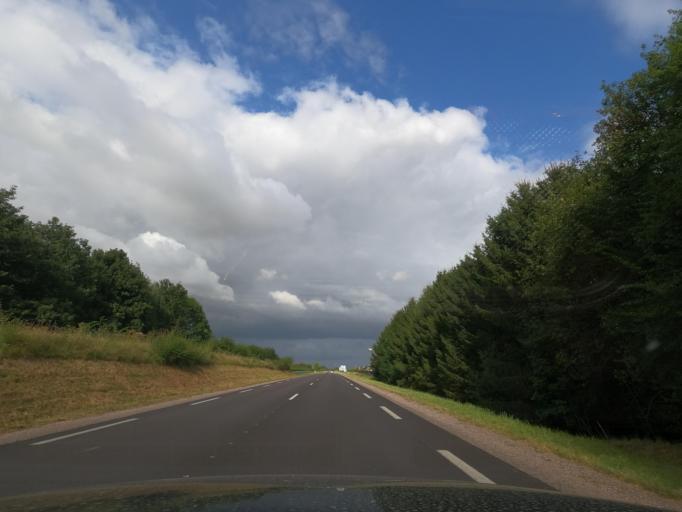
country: FR
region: Haute-Normandie
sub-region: Departement de l'Eure
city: Bernay
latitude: 49.1068
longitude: 0.5839
